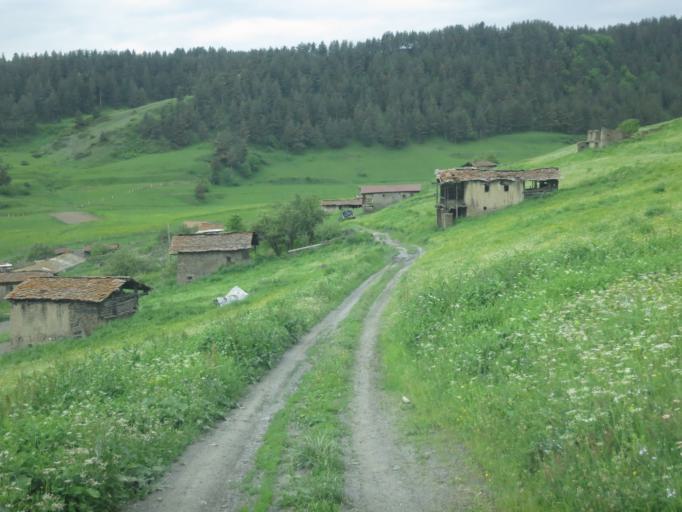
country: RU
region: Chechnya
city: Itum-Kali
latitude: 42.3750
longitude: 45.6604
